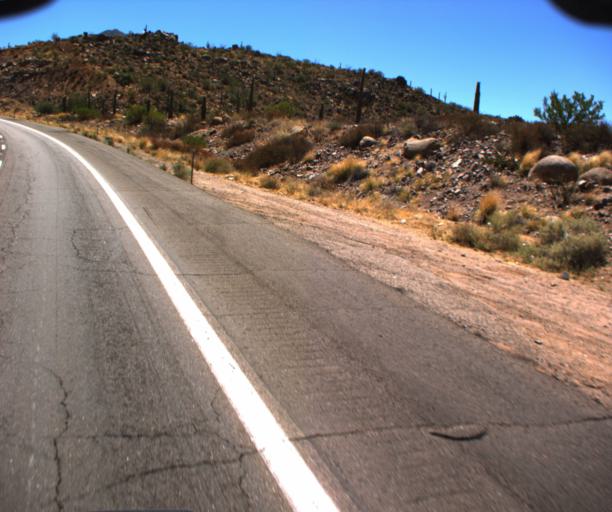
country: US
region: Arizona
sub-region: Gila County
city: Tonto Basin
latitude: 33.8166
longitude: -111.4823
